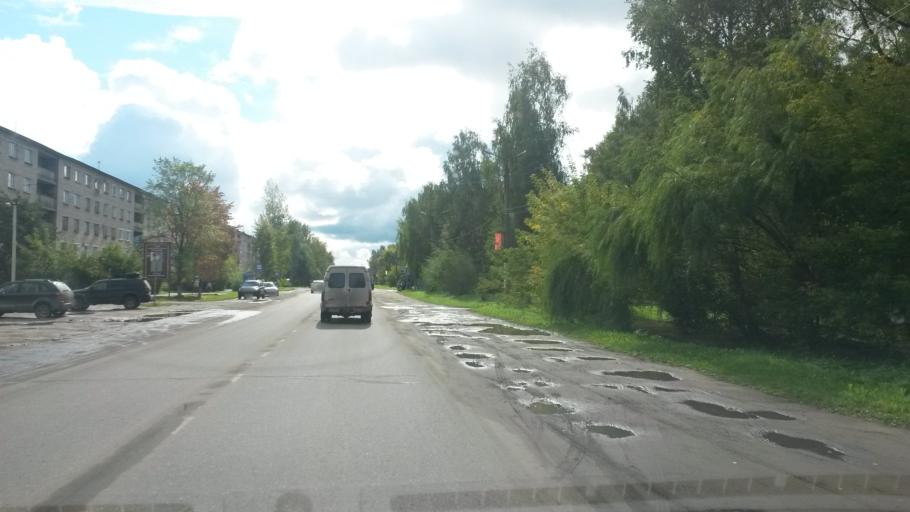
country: RU
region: Ivanovo
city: Zavolzhsk
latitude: 57.4878
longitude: 42.1414
